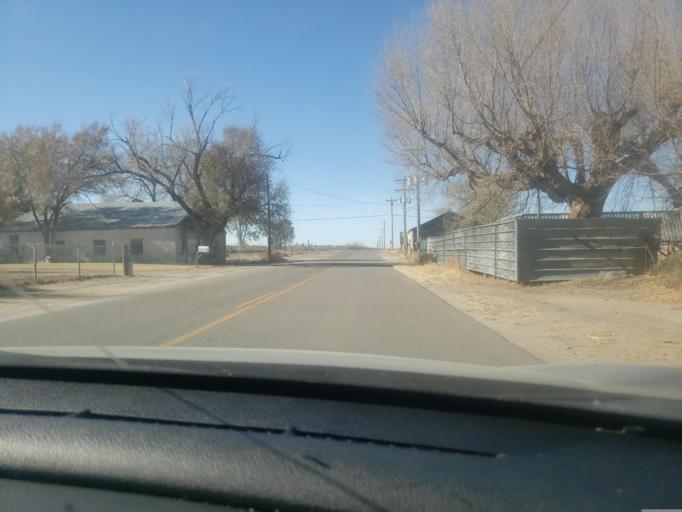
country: US
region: Kansas
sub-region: Finney County
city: Garden City
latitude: 37.9516
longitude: -100.8769
